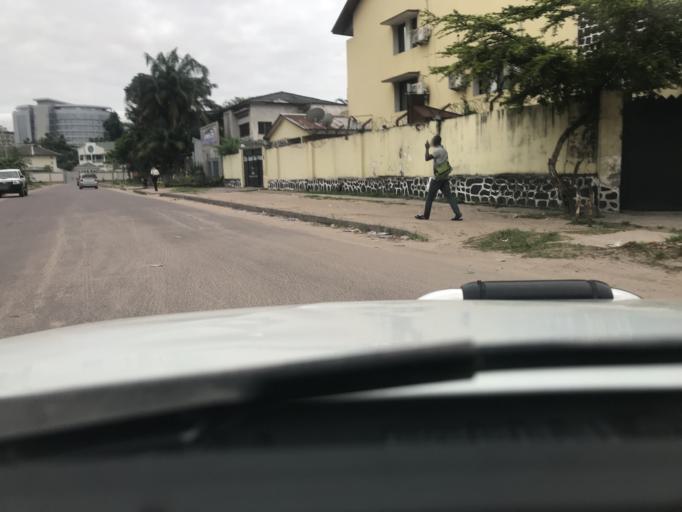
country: CD
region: Kinshasa
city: Kinshasa
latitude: -4.3147
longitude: 15.2866
